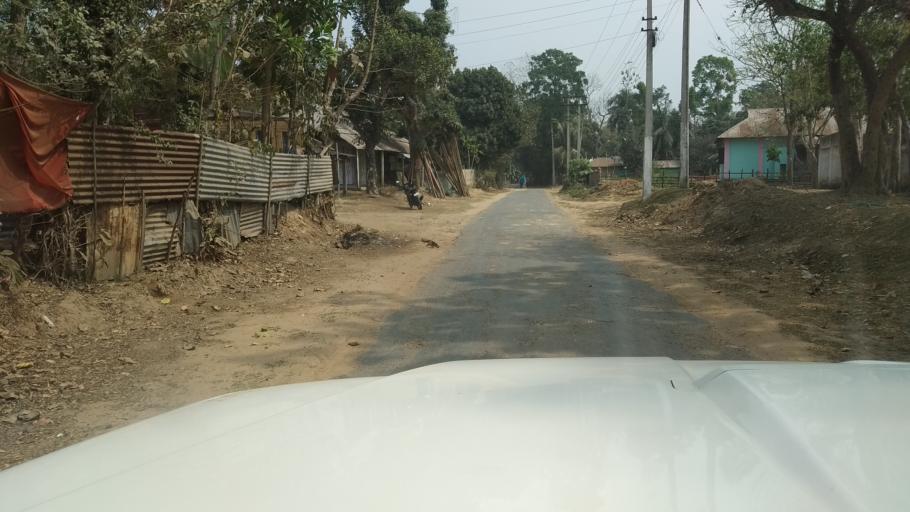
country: IN
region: Tripura
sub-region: West Tripura
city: Sonamura
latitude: 23.4192
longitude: 91.2862
